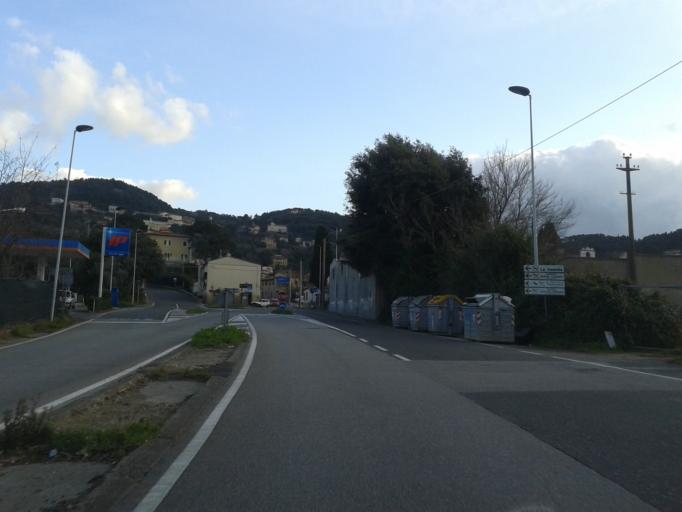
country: IT
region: Tuscany
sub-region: Provincia di Livorno
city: Livorno
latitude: 43.5004
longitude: 10.3420
